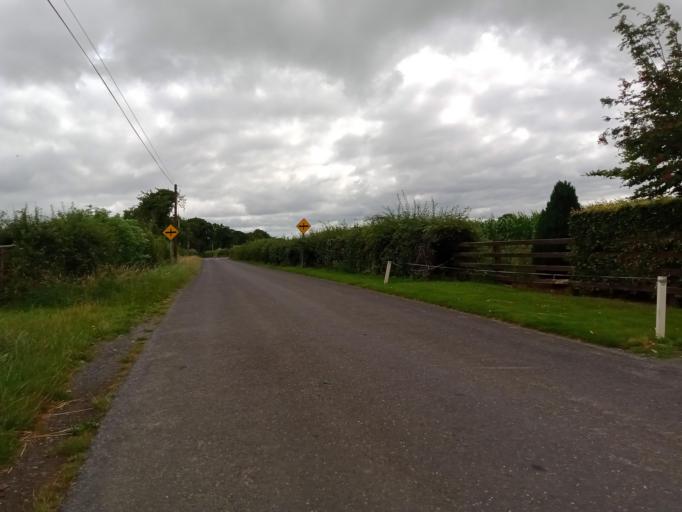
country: IE
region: Leinster
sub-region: Kilkenny
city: Callan
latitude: 52.5768
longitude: -7.3786
